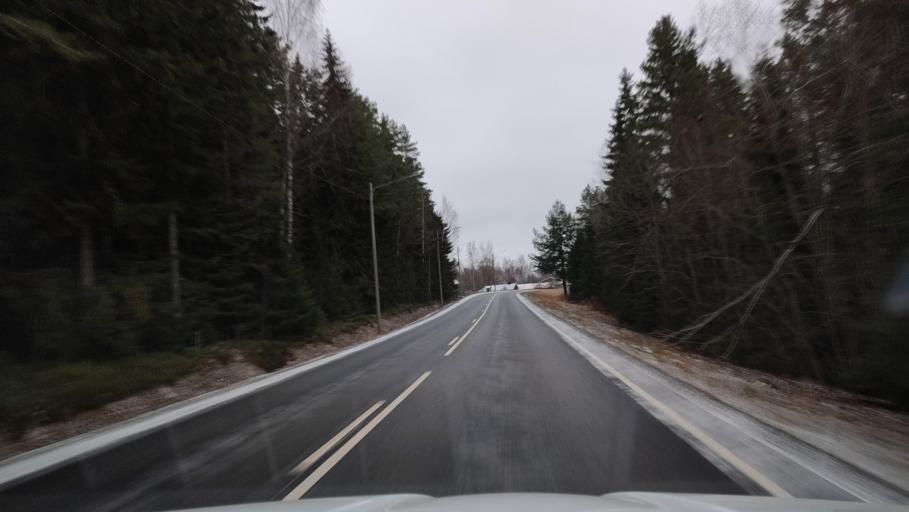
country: FI
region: Southern Ostrobothnia
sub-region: Suupohja
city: Karijoki
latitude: 62.2995
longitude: 21.6834
